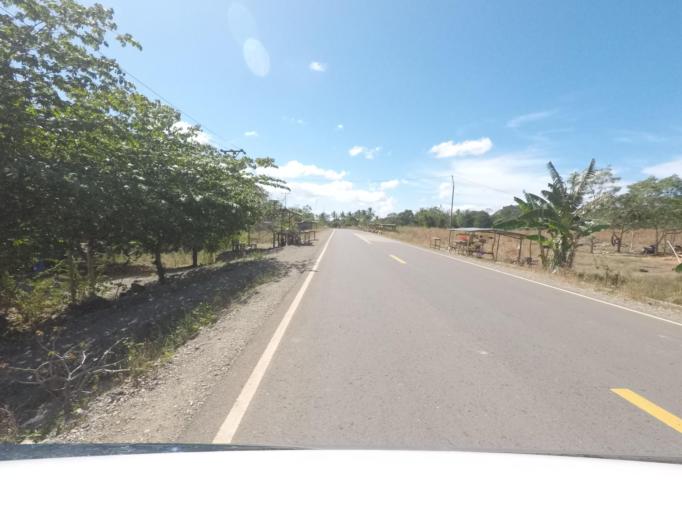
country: TL
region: Baucau
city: Baucau
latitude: -8.4906
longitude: 126.3667
